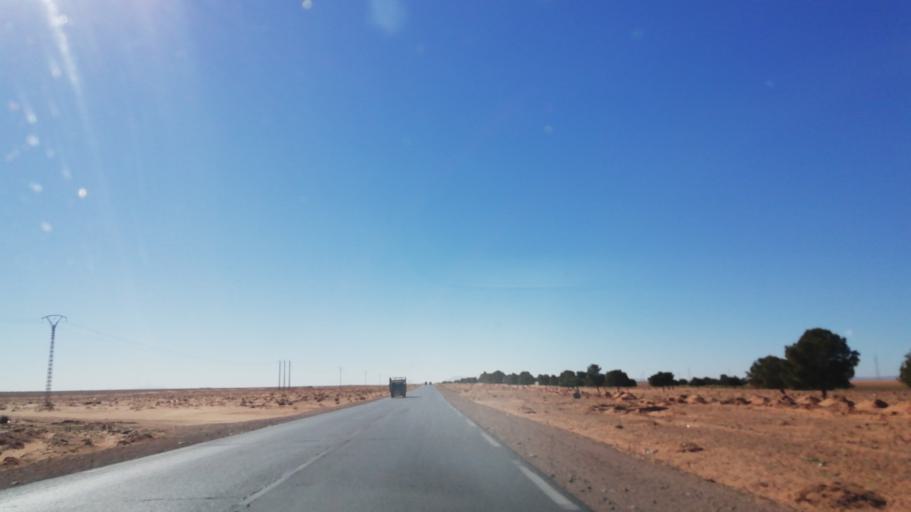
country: DZ
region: Wilaya de Naama
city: Naama
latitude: 33.9756
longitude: 0.0245
